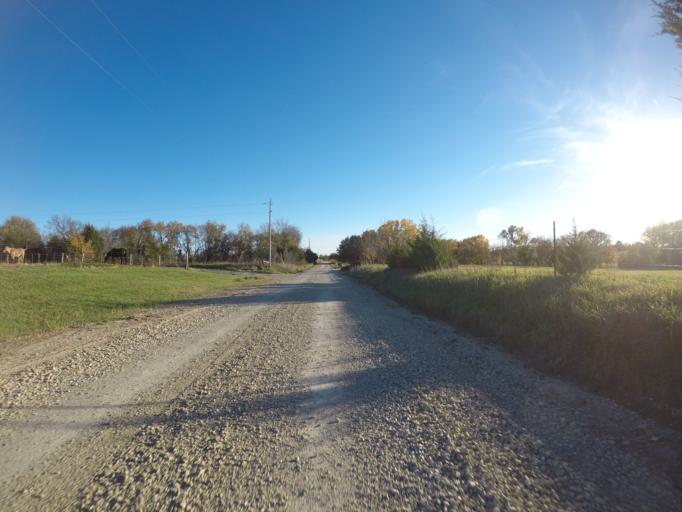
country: US
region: Kansas
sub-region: Riley County
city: Manhattan
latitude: 39.2730
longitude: -96.7051
